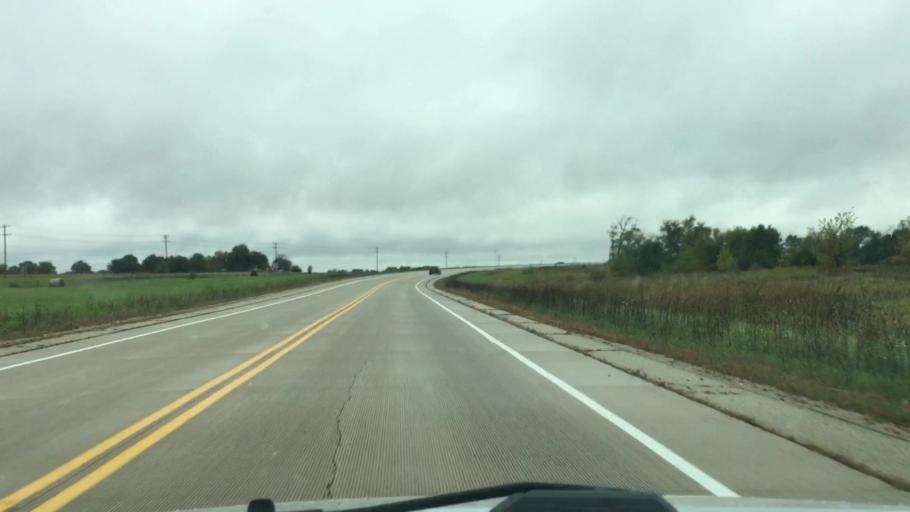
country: US
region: Wisconsin
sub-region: Walworth County
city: Whitewater
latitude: 42.8177
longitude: -88.7291
